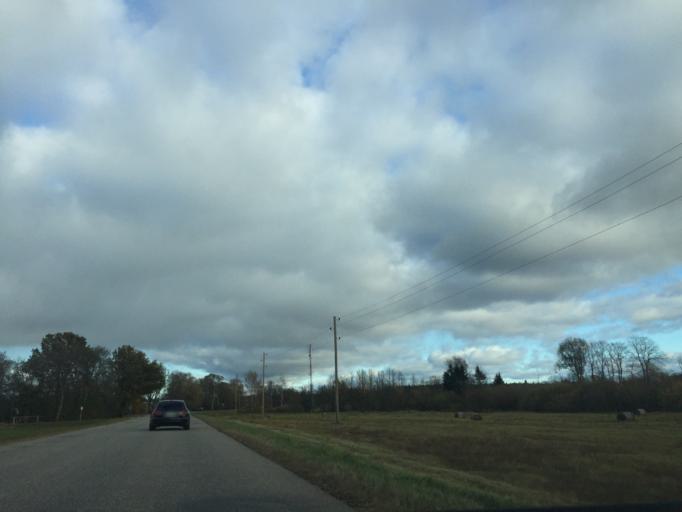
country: LV
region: Carnikava
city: Carnikava
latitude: 57.1159
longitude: 24.3109
